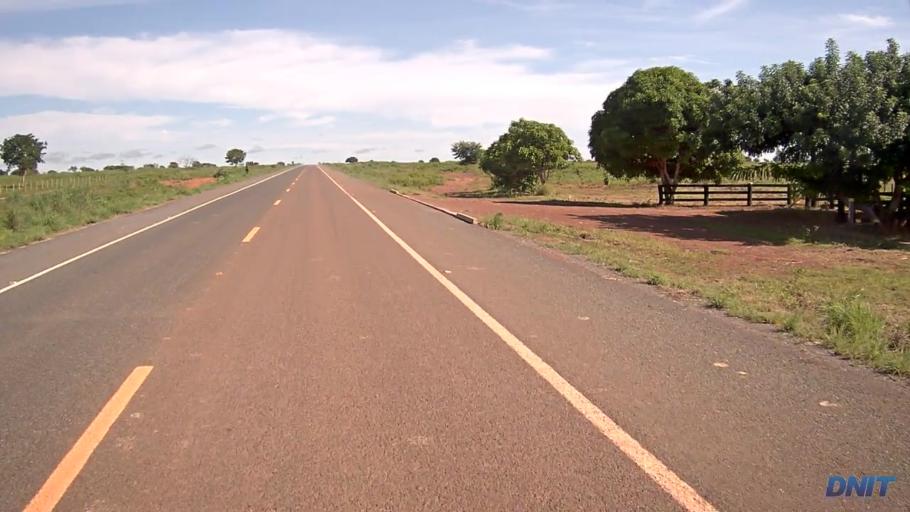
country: BR
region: Goias
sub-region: Sao Miguel Do Araguaia
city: Sao Miguel do Araguaia
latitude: -13.4935
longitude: -50.1083
